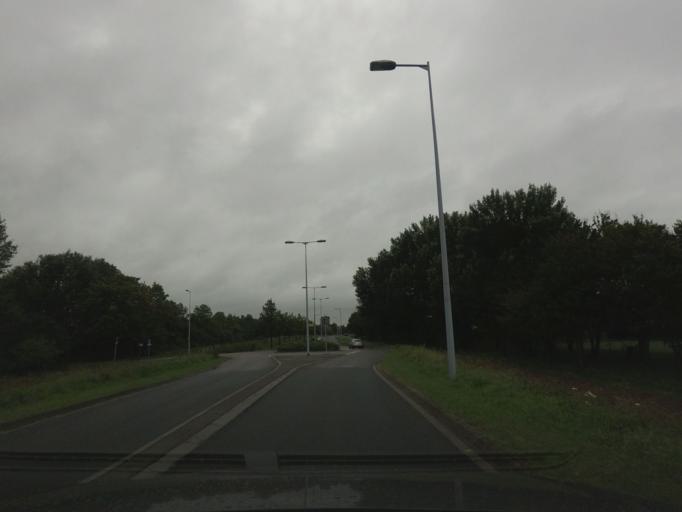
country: NL
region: North Holland
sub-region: Gemeente Haarlemmermeer
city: Hoofddorp
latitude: 52.3103
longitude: 4.6490
